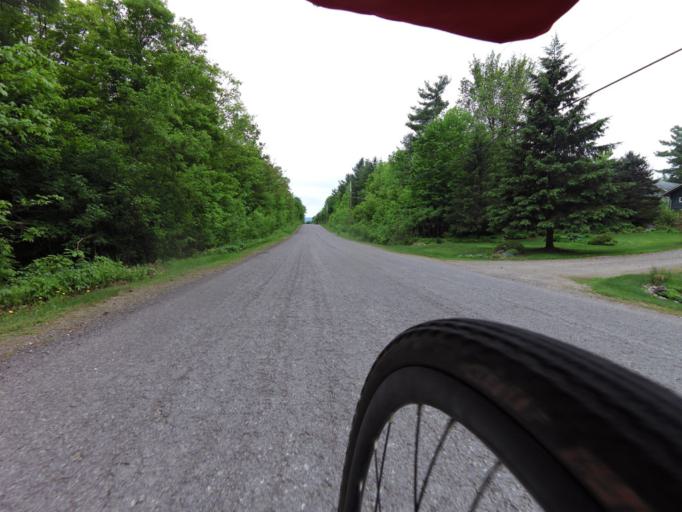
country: CA
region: Ontario
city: Renfrew
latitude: 45.2955
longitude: -76.7172
